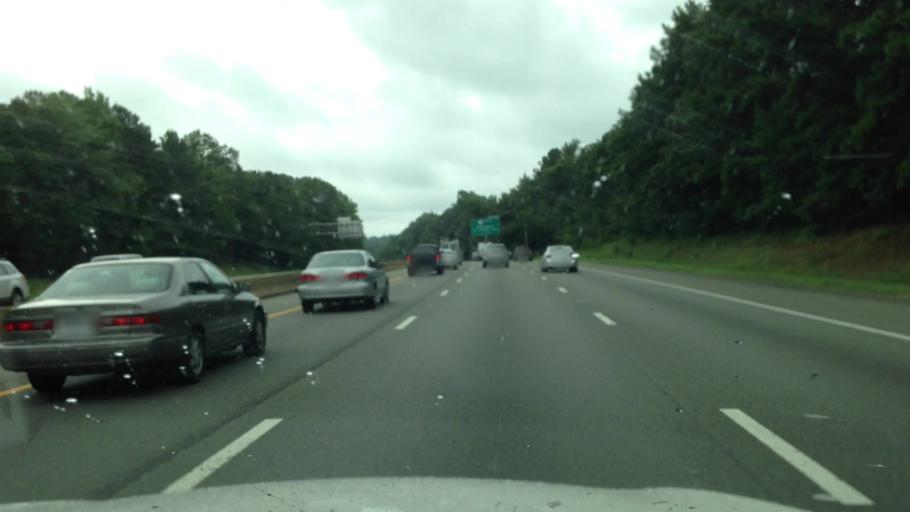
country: US
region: Virginia
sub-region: Chesterfield County
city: Chester
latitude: 37.3868
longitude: -77.4195
